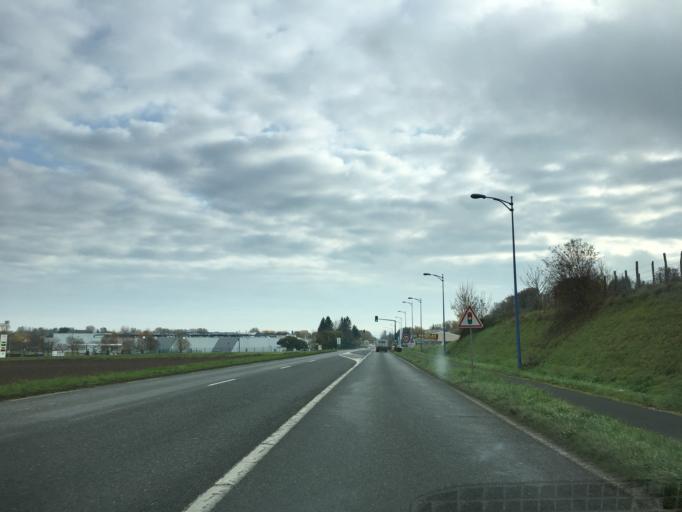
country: FR
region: Bourgogne
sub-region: Departement de l'Yonne
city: Pont-sur-Yonne
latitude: 48.2952
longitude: 3.1930
